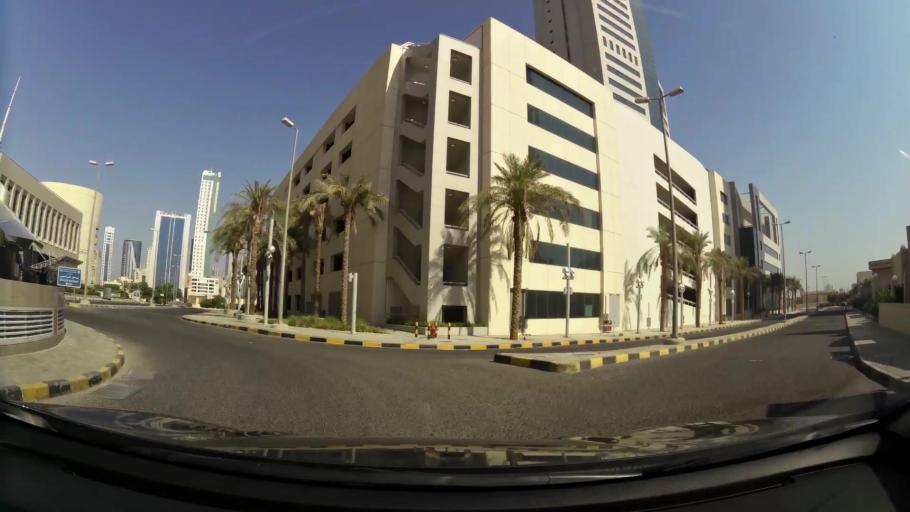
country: KW
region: Al Asimah
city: Kuwait City
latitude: 29.3633
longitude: 47.9824
